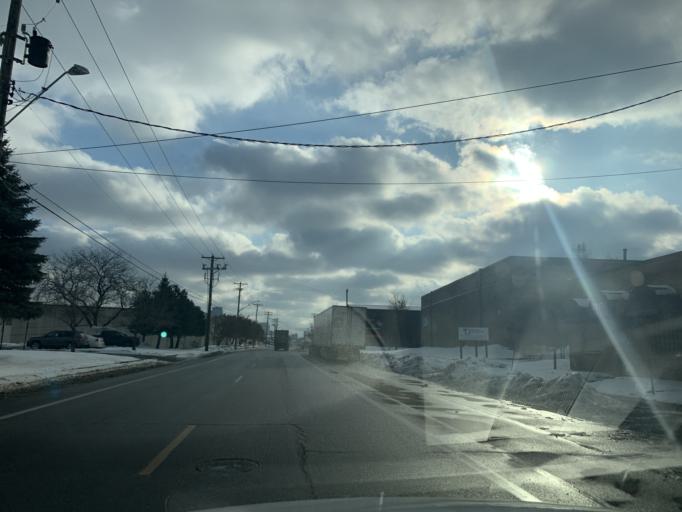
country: US
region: Minnesota
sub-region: Hennepin County
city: Minneapolis
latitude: 45.0092
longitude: -93.2804
